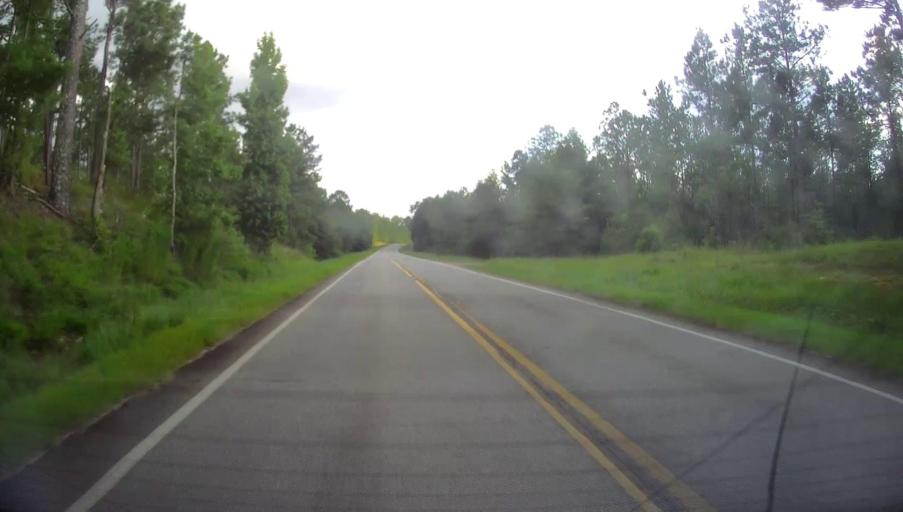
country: US
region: Georgia
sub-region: Crawford County
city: Roberta
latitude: 32.8182
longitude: -84.0228
